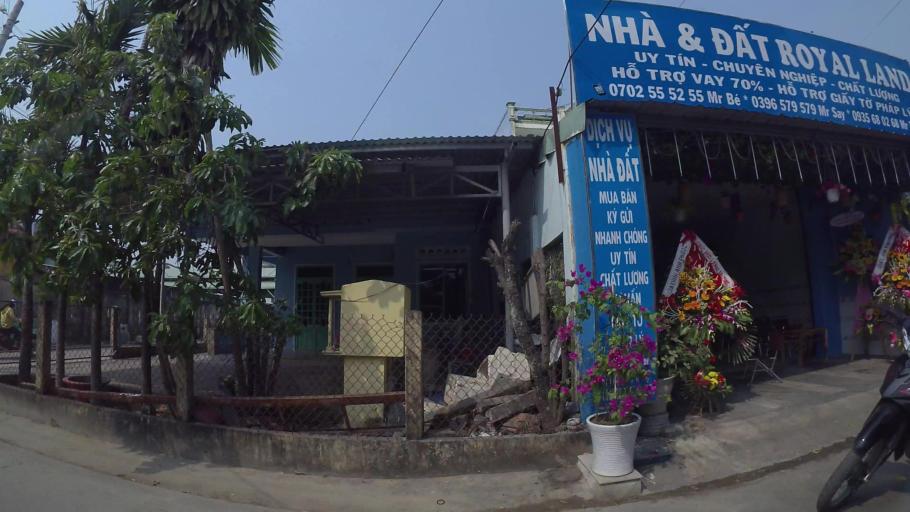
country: VN
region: Da Nang
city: Ngu Hanh Son
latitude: 15.9934
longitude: 108.2390
